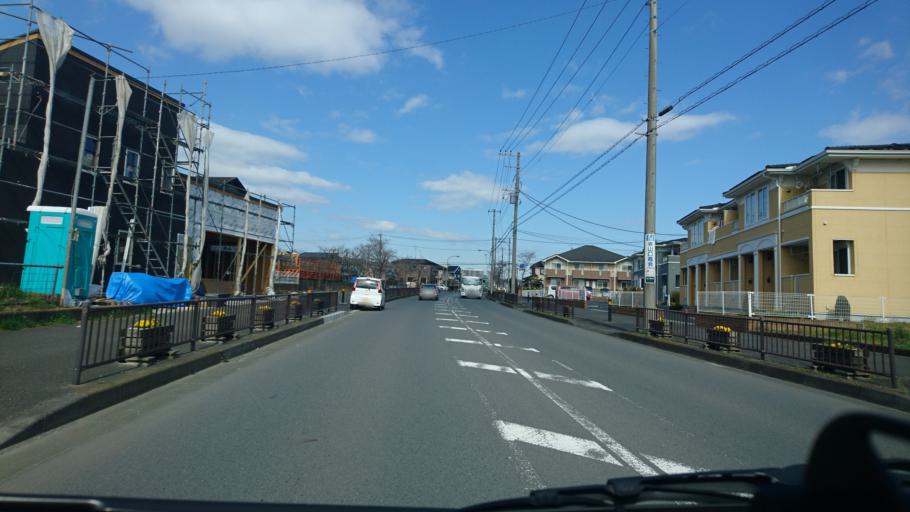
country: JP
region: Kanagawa
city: Zama
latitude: 35.5294
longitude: 139.3341
